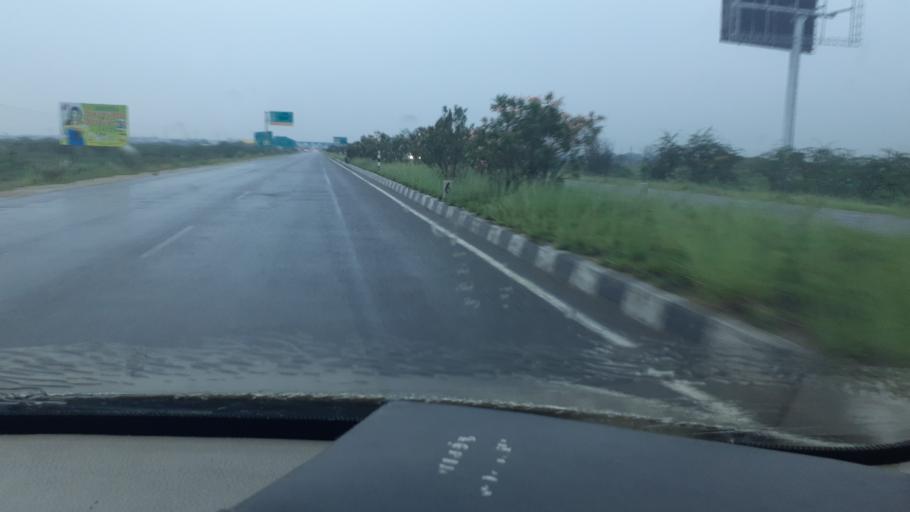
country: IN
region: Tamil Nadu
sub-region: Virudhunagar
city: Sattur
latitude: 9.3909
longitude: 77.9152
